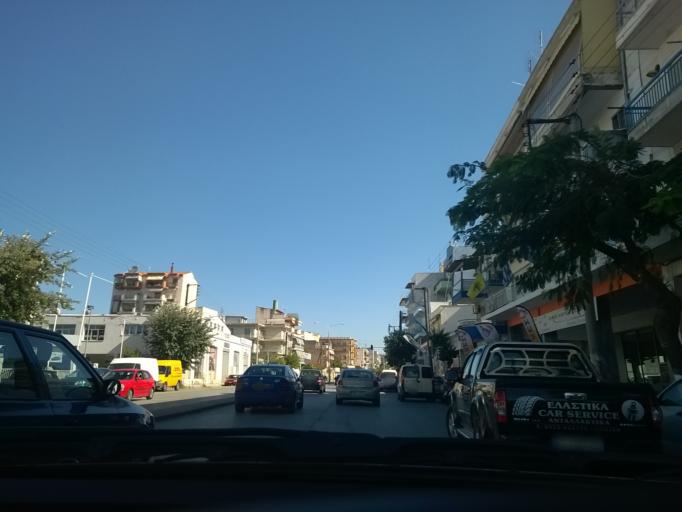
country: GR
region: Central Macedonia
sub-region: Nomos Thessalonikis
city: Ampelokipoi
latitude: 40.6520
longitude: 22.9130
